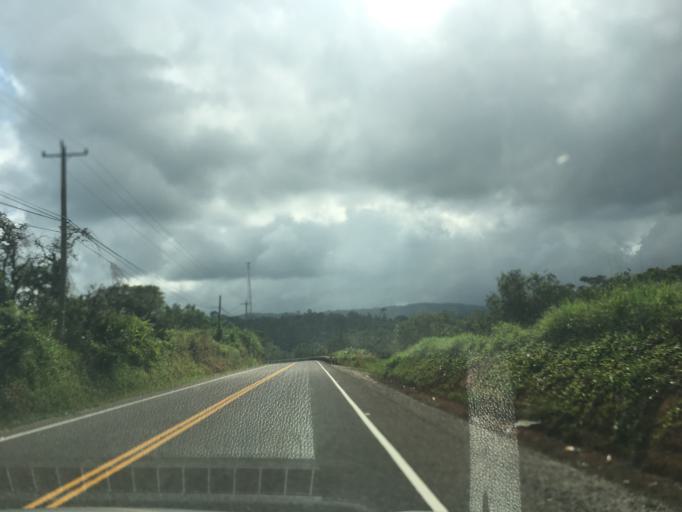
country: BZ
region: Stann Creek
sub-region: Dangriga
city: Dangriga
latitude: 16.9949
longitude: -88.4073
